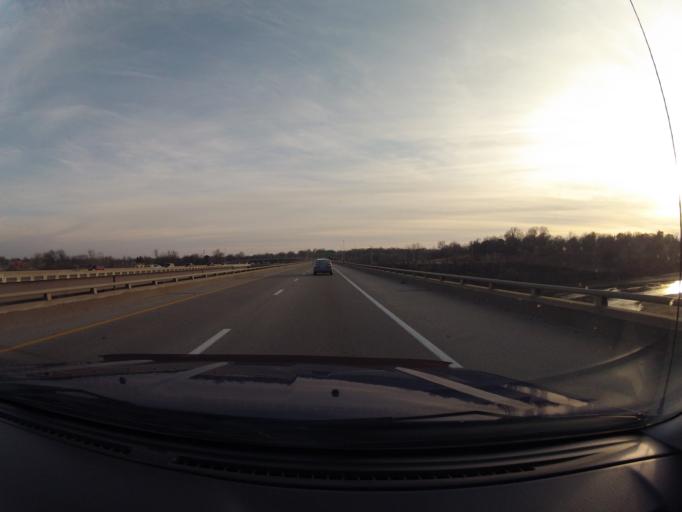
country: US
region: Kansas
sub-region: Shawnee County
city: Topeka
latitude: 39.0711
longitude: -95.7315
